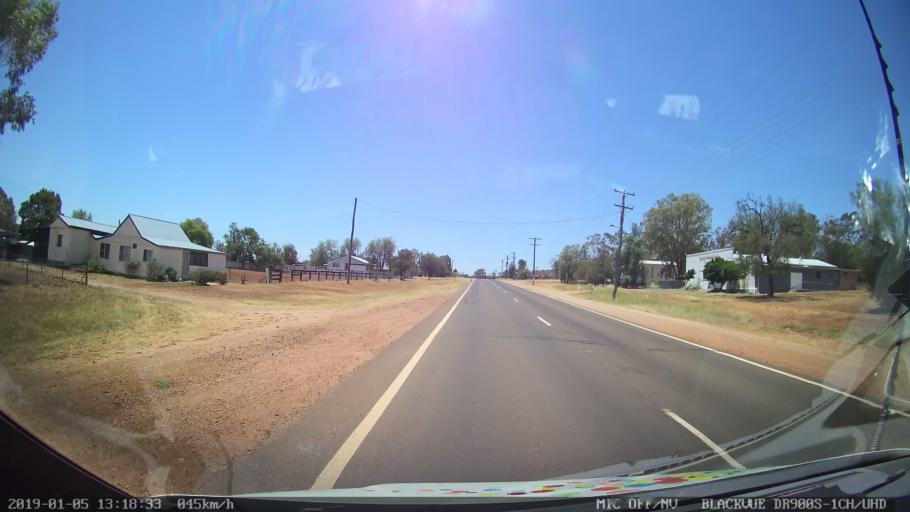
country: AU
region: New South Wales
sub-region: Gunnedah
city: Gunnedah
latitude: -31.0972
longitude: 149.9116
